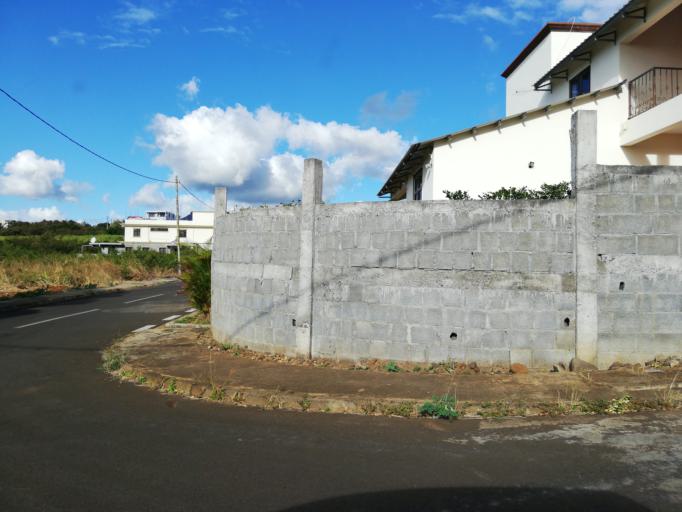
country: MU
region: Black River
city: Petite Riviere
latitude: -20.1996
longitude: 57.4625
